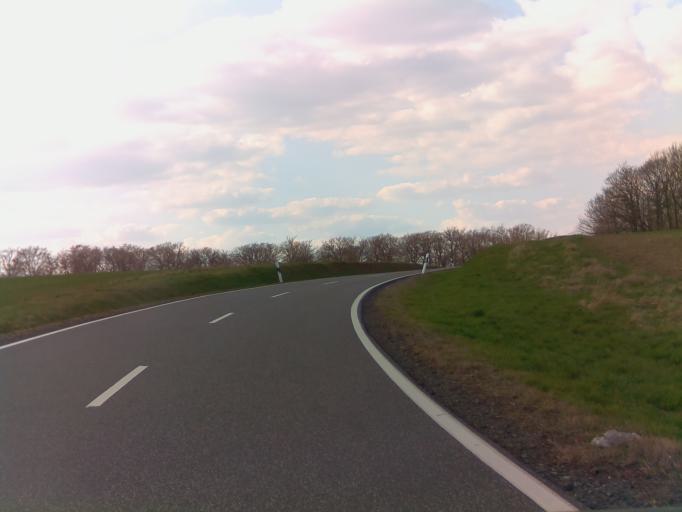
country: DE
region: Rheinland-Pfalz
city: Limbach
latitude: 49.7259
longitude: 7.5448
